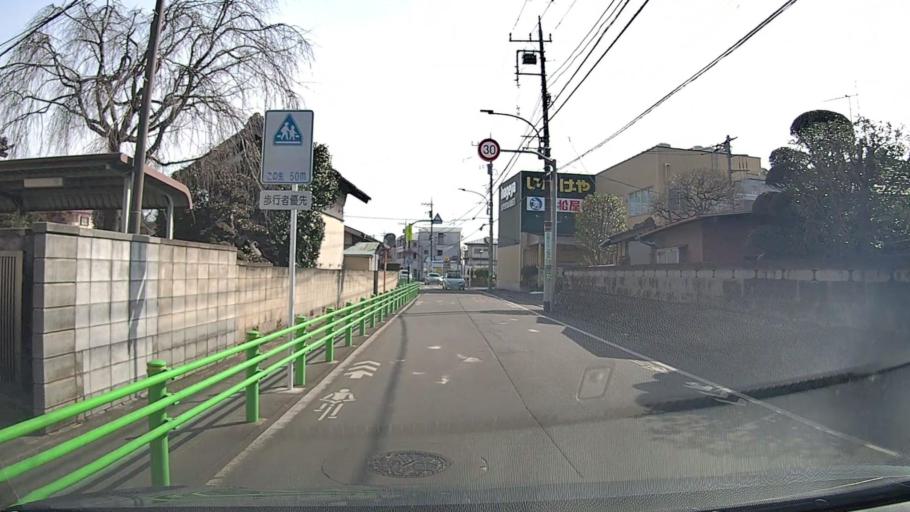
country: JP
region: Tokyo
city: Nishi-Tokyo-shi
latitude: 35.7458
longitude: 139.5710
